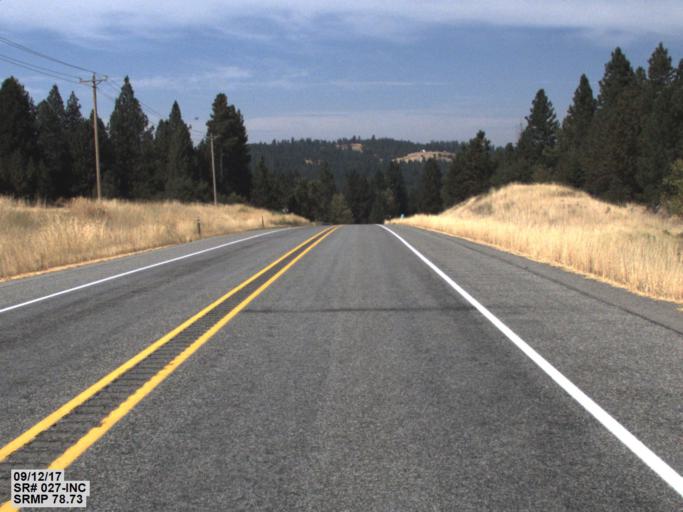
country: US
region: Washington
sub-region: Spokane County
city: Veradale
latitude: 47.5659
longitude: -117.2175
